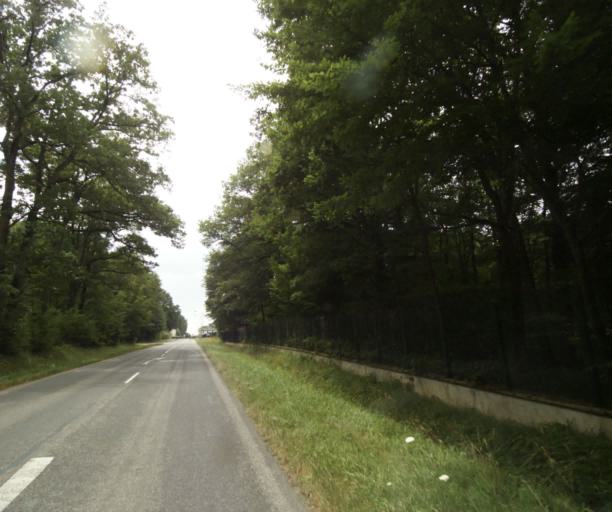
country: FR
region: Centre
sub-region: Departement du Loiret
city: Semoy
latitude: 47.9464
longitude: 1.9490
